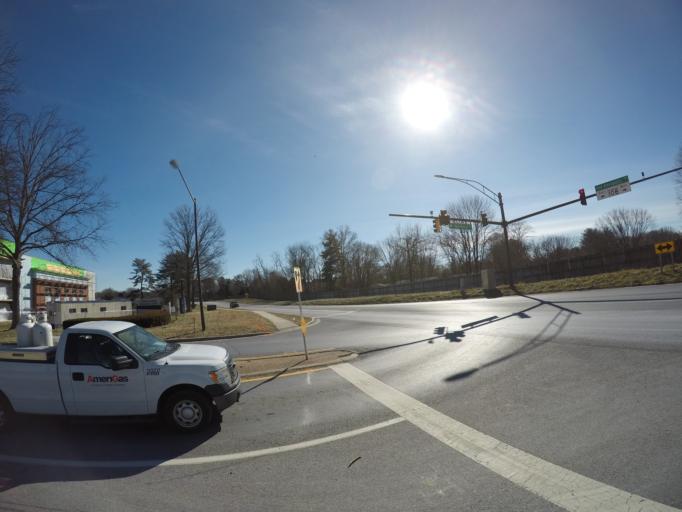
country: US
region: Maryland
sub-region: Howard County
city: Columbia
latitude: 39.2300
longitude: -76.8284
